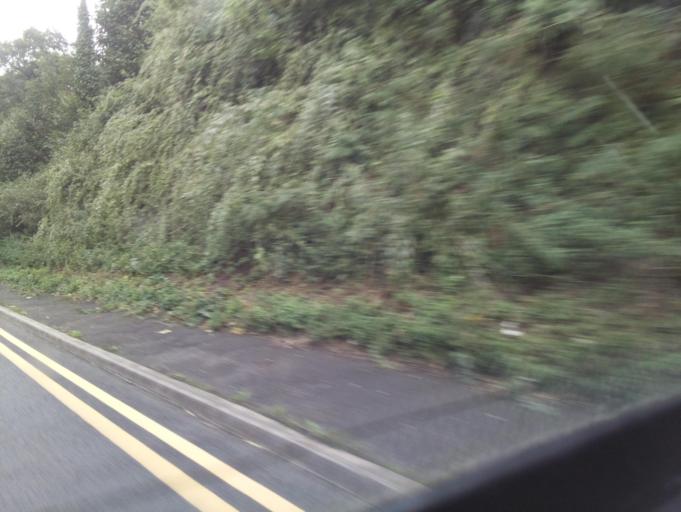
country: GB
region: England
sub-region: Shropshire
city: Bridgnorth
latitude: 52.5402
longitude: -2.4098
